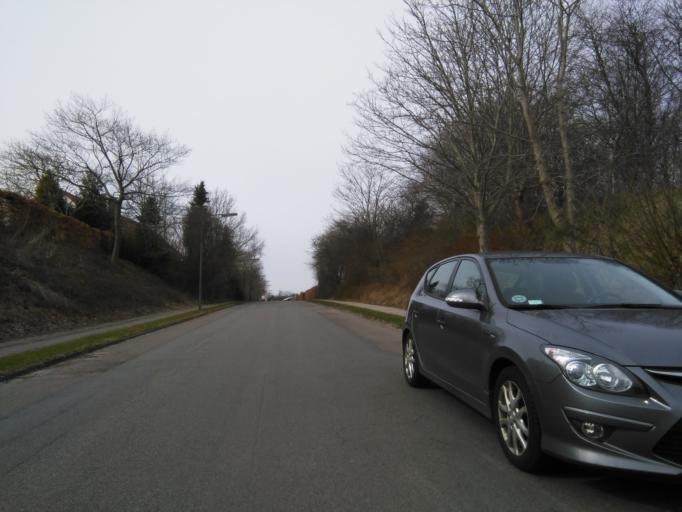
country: DK
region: Central Jutland
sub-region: Arhus Kommune
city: Beder
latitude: 56.1033
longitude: 10.2198
